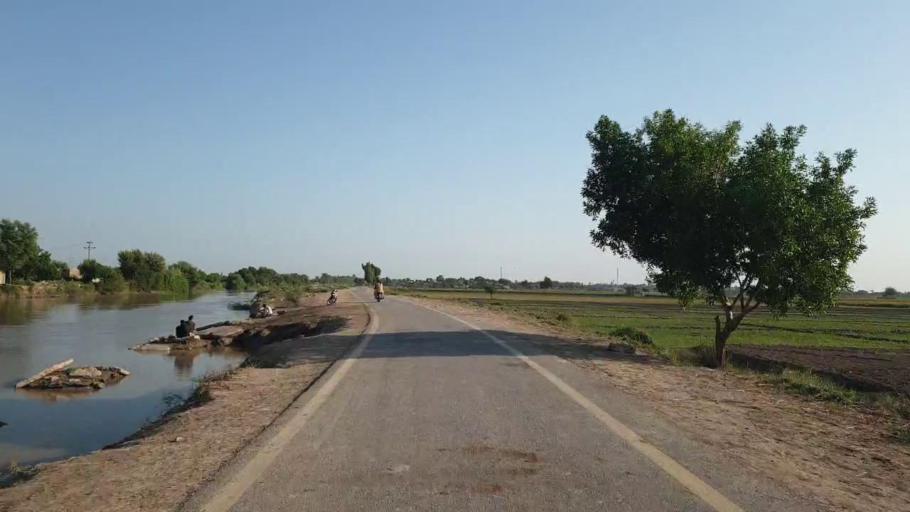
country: PK
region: Sindh
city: Hyderabad
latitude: 25.3285
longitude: 68.4247
